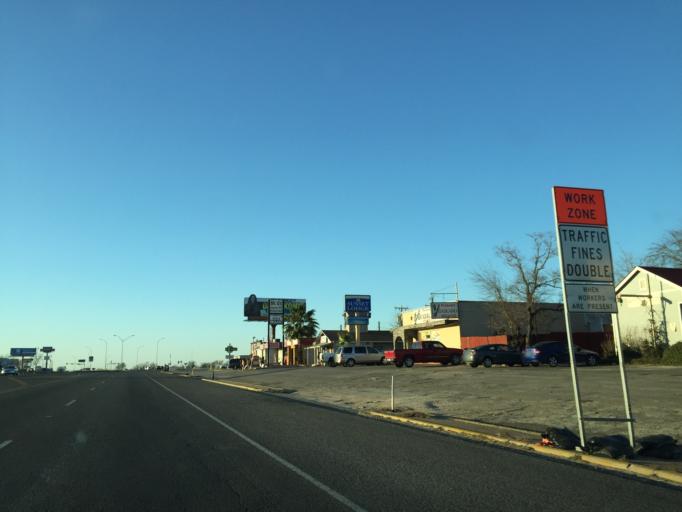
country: US
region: Texas
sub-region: Bastrop County
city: Elgin
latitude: 30.3477
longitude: -97.3833
